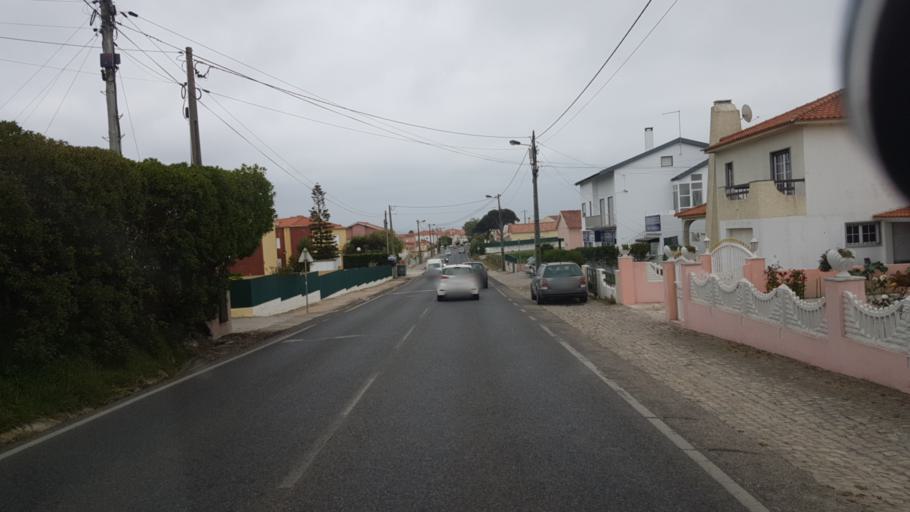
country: PT
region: Lisbon
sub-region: Torres Vedras
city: Silveira
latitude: 39.1180
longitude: -9.3723
